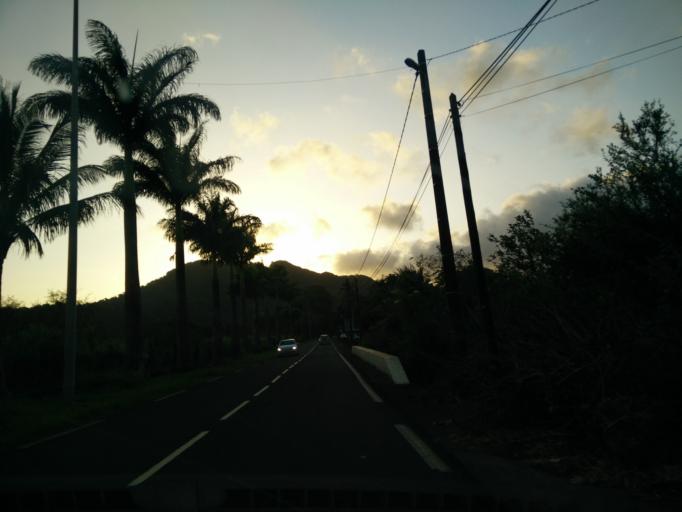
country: MQ
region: Martinique
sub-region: Martinique
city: Le Morne-Rouge
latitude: 14.7618
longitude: -61.1155
